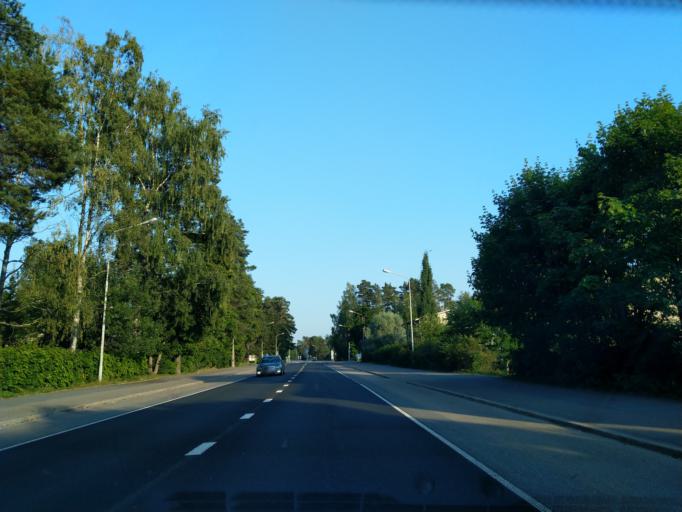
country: FI
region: Satakunta
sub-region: Pohjois-Satakunta
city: Kankaanpaeae
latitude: 61.8102
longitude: 22.3822
